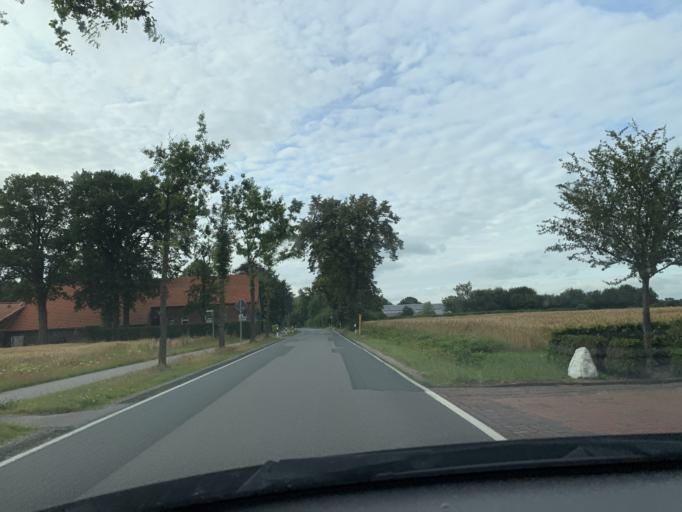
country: DE
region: Lower Saxony
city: Westerstede
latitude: 53.2817
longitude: 7.9257
